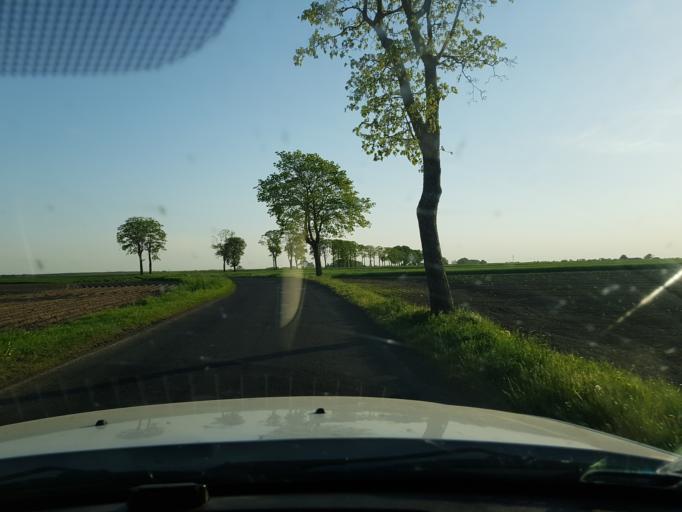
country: PL
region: West Pomeranian Voivodeship
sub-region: Powiat goleniowski
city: Mosty
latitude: 53.4755
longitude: 14.9617
